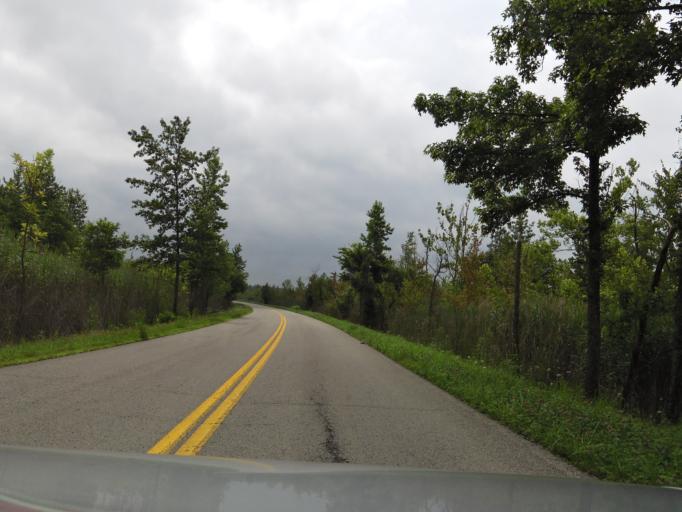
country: US
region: Kentucky
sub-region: Muhlenberg County
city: Morehead
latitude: 37.2990
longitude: -87.3200
